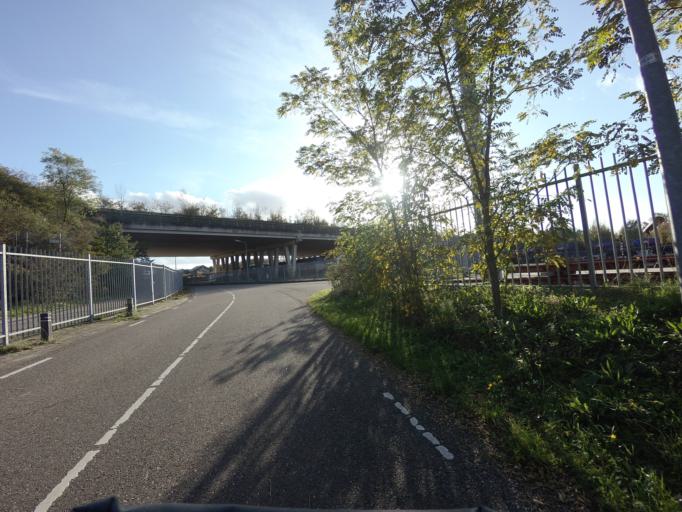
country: NL
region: North Holland
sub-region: Gemeente Bussum
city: Bussum
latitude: 52.2529
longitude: 5.1699
